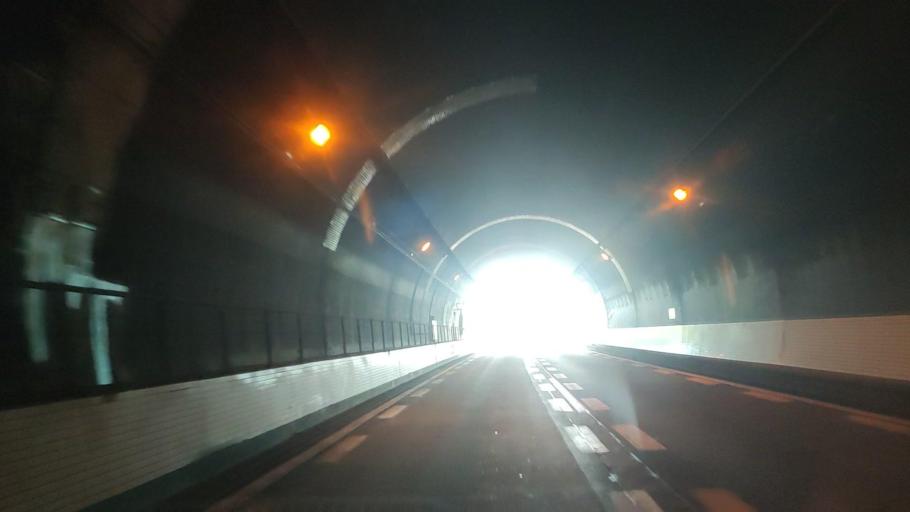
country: JP
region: Niigata
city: Joetsu
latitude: 37.1675
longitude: 138.1048
